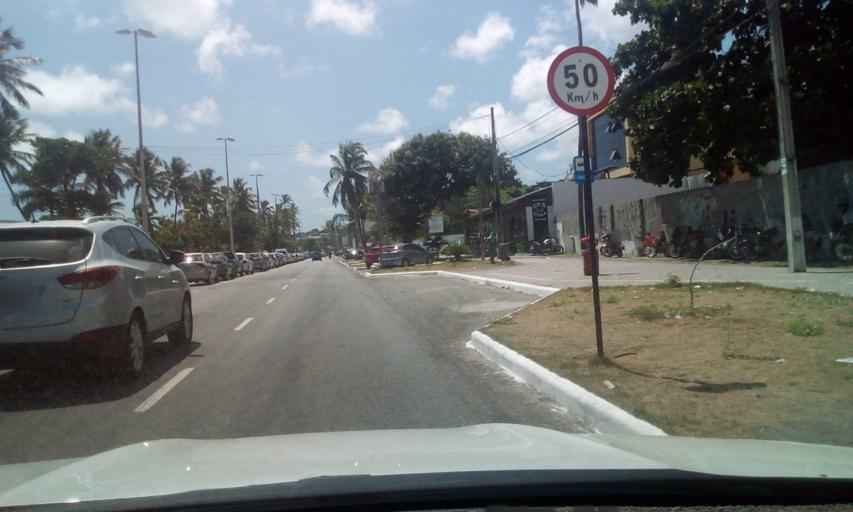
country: BR
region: Paraiba
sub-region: Joao Pessoa
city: Joao Pessoa
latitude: -7.1297
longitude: -34.8226
